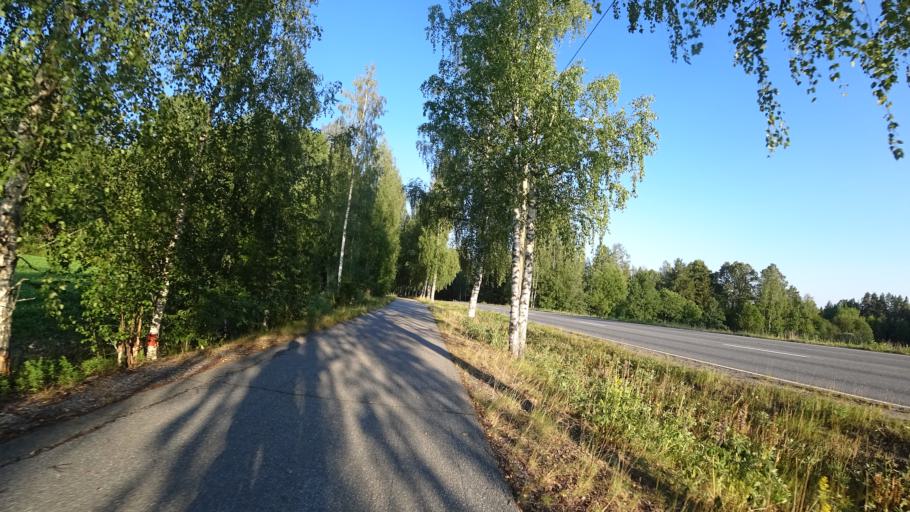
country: FI
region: Pirkanmaa
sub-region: Tampere
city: Nokia
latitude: 61.4716
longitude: 23.3844
